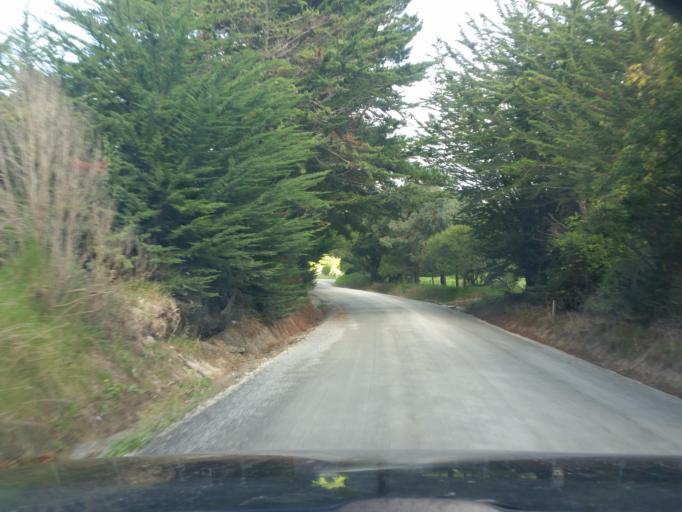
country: NZ
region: Northland
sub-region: Kaipara District
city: Dargaville
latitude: -35.9987
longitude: 173.9484
